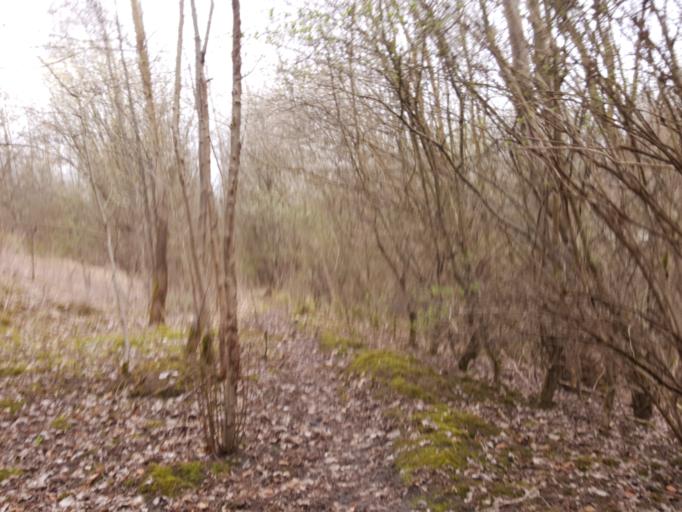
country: DE
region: Hamburg
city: Wandsbek
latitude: 53.5070
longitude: 10.1055
